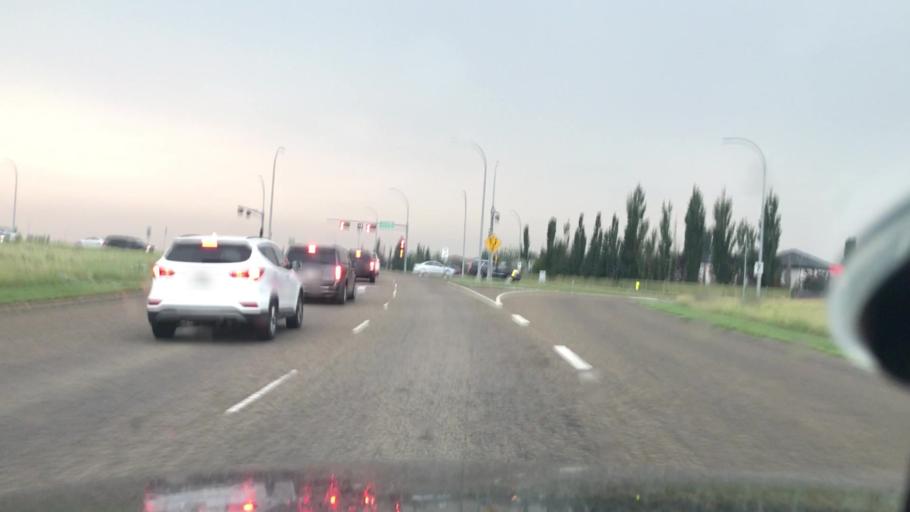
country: CA
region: Alberta
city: Edmonton
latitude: 53.4586
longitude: -113.5897
